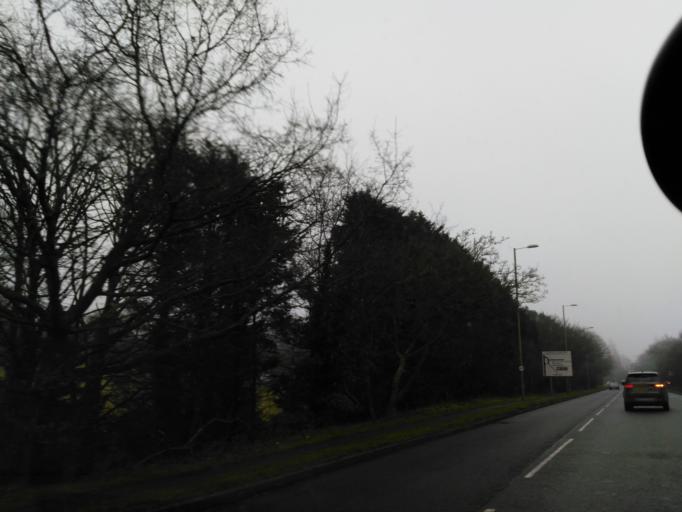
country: GB
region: England
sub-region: Hampshire
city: Lee-on-the-Solent
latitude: 50.8378
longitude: -1.2244
